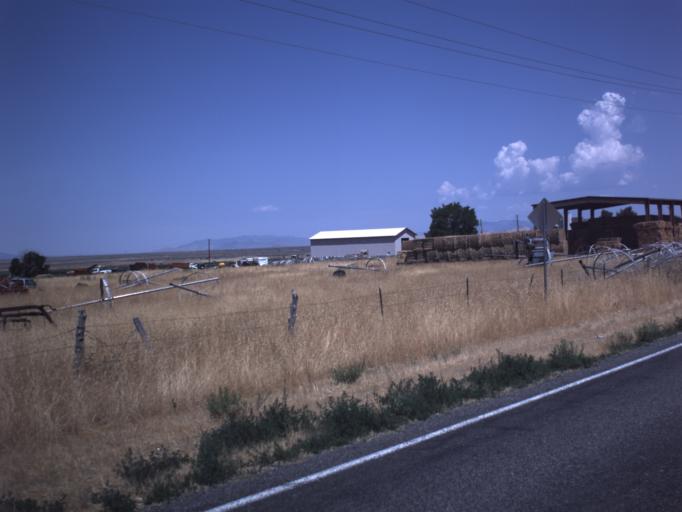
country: US
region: Utah
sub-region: Millard County
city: Delta
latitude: 39.4006
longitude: -112.3350
